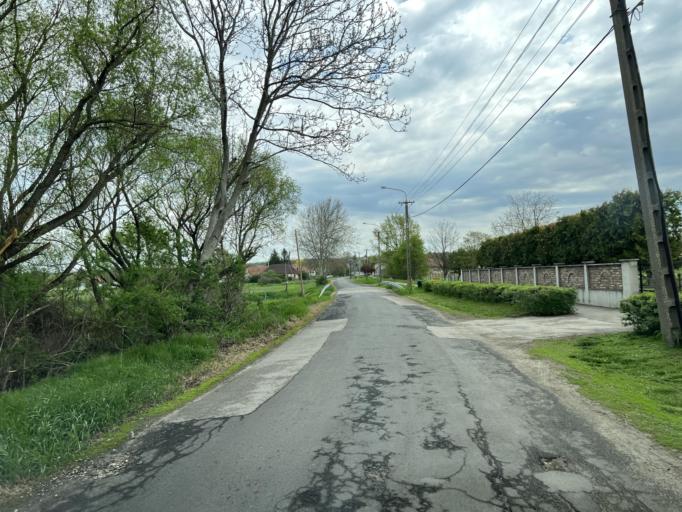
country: HU
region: Pest
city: Cegledbercel
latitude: 47.2190
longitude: 19.6618
